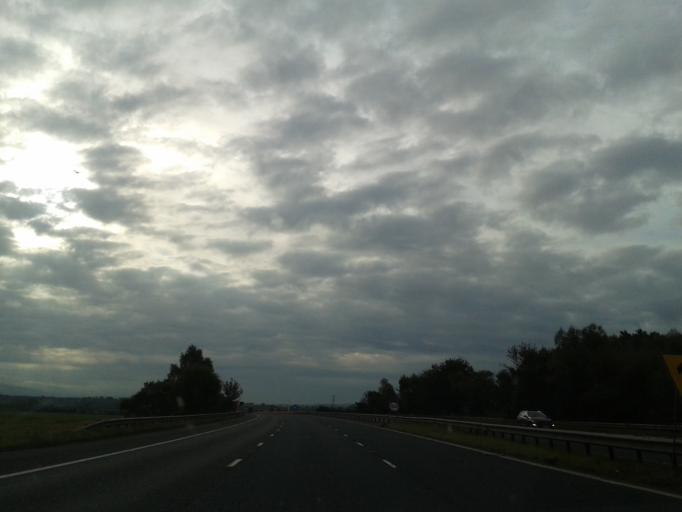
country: GB
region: England
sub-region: Cumbria
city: Scotby
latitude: 54.9121
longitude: -2.8998
